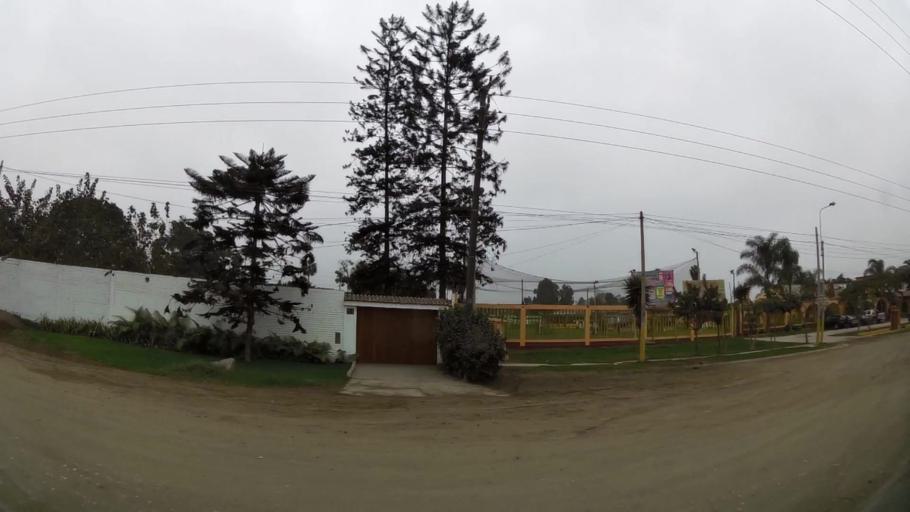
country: PE
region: Lima
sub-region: Lima
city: Punta Hermosa
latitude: -12.2530
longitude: -76.8922
